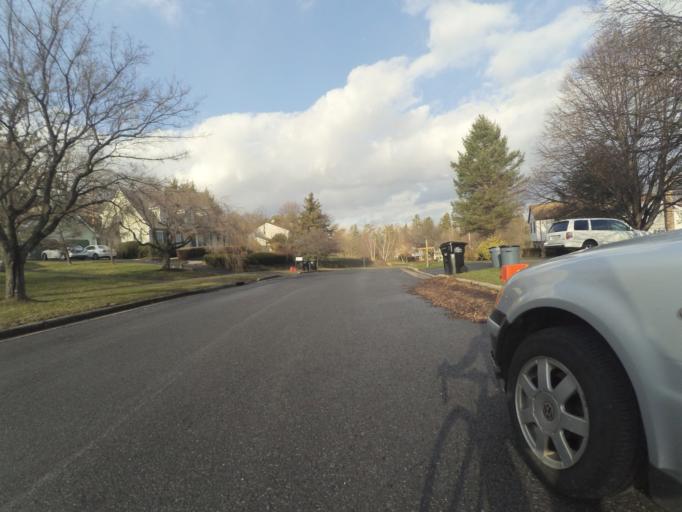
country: US
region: Pennsylvania
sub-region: Centre County
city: Lemont
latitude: 40.7915
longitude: -77.8347
